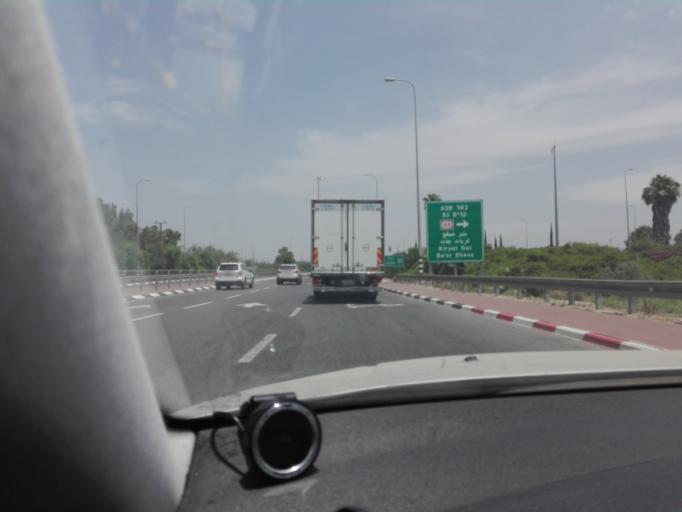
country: IL
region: Central District
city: Bene 'Ayish
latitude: 31.7320
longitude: 34.7563
